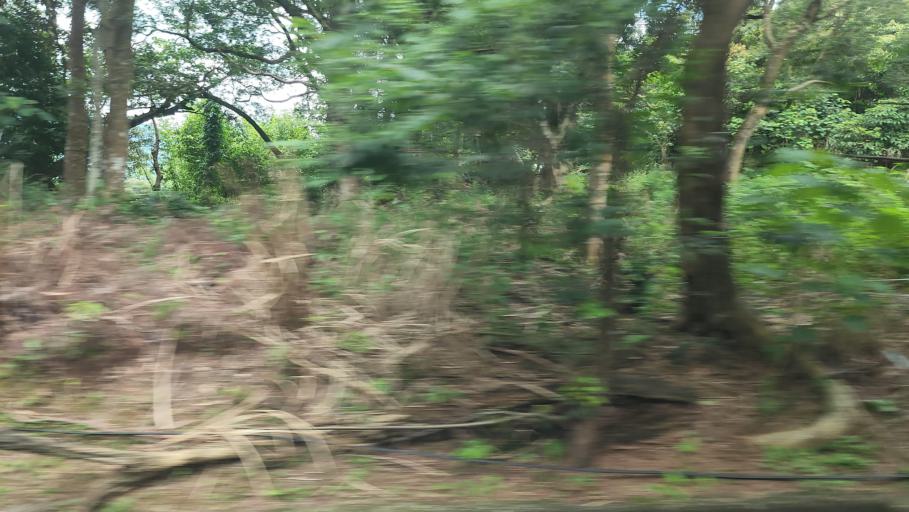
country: TW
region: Taiwan
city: Daxi
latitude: 24.8741
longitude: 121.4142
